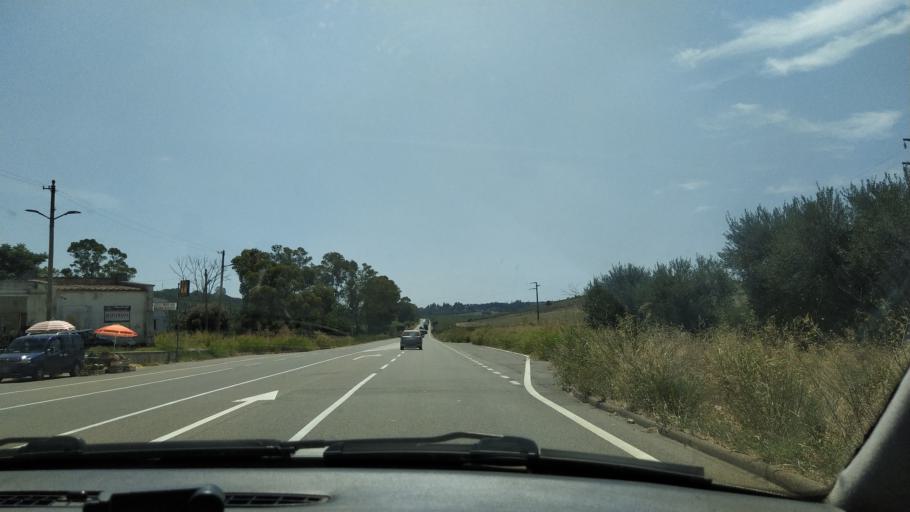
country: IT
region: Basilicate
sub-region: Provincia di Matera
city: Bernalda
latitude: 40.4441
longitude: 16.7804
